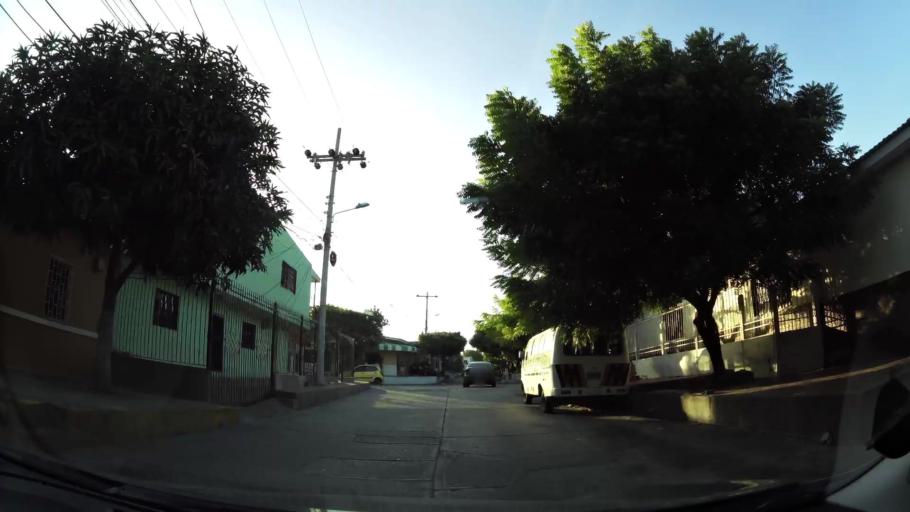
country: CO
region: Atlantico
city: Barranquilla
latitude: 10.9671
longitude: -74.7946
